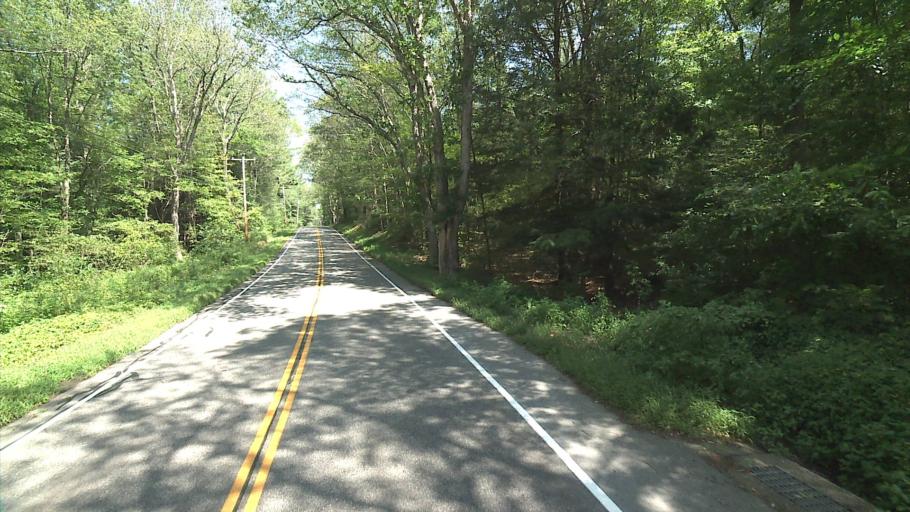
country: US
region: Connecticut
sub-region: Windham County
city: South Woodstock
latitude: 41.9078
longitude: -72.0781
